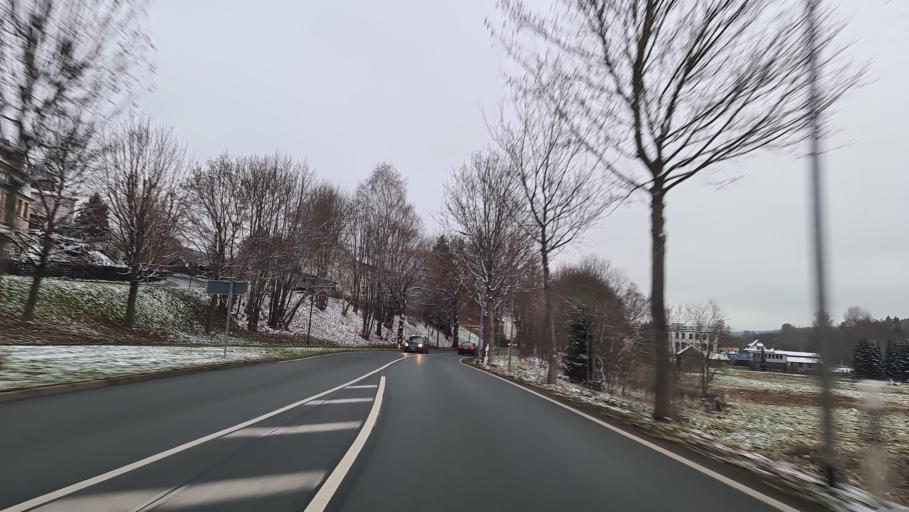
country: DE
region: Saxony
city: Adorf
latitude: 50.3177
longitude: 12.2721
